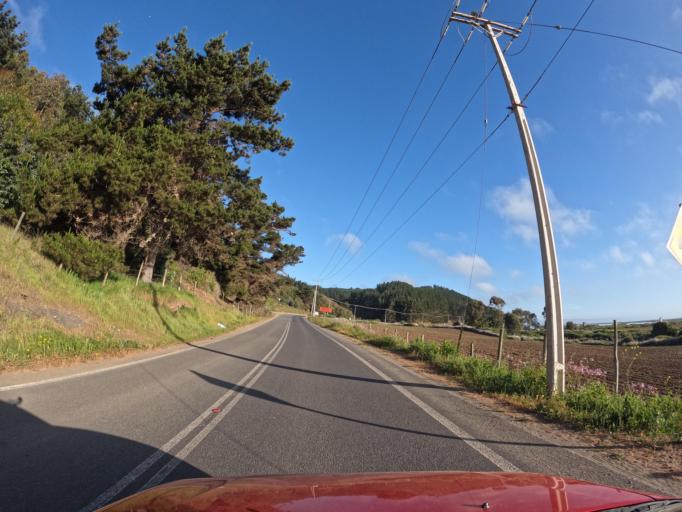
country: CL
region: Maule
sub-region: Provincia de Talca
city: Constitucion
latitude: -34.9839
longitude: -72.1795
